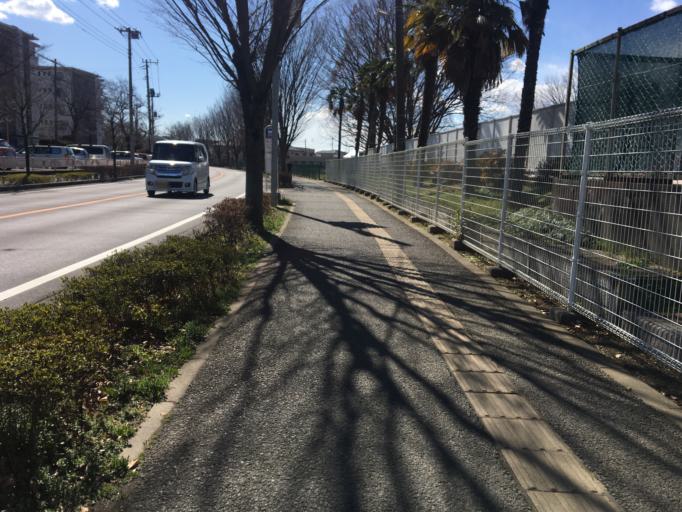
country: JP
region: Saitama
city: Shiki
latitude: 35.8191
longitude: 139.5553
